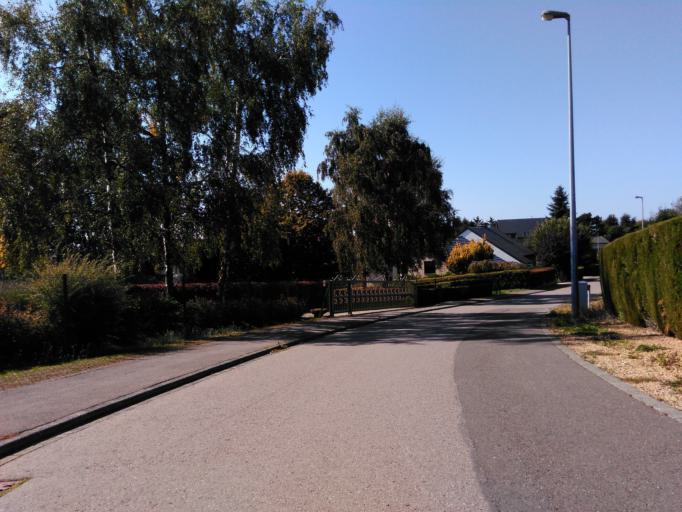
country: BE
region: Wallonia
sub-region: Province du Luxembourg
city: Martelange
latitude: 49.8291
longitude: 5.7642
